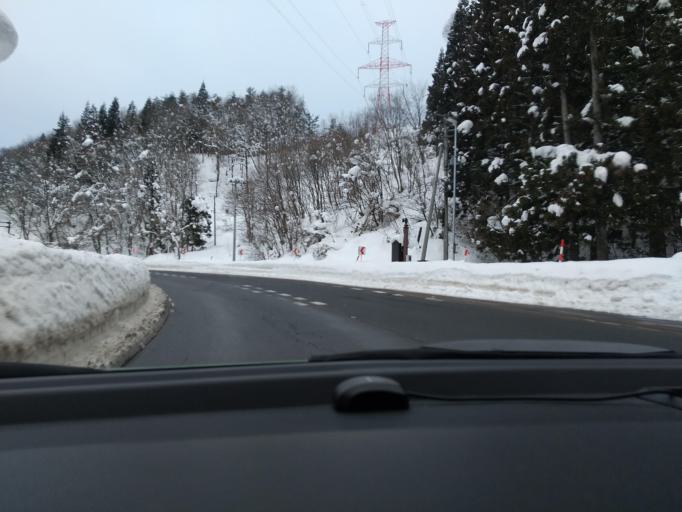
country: JP
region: Akita
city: Kakunodatemachi
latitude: 39.6783
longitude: 140.7007
